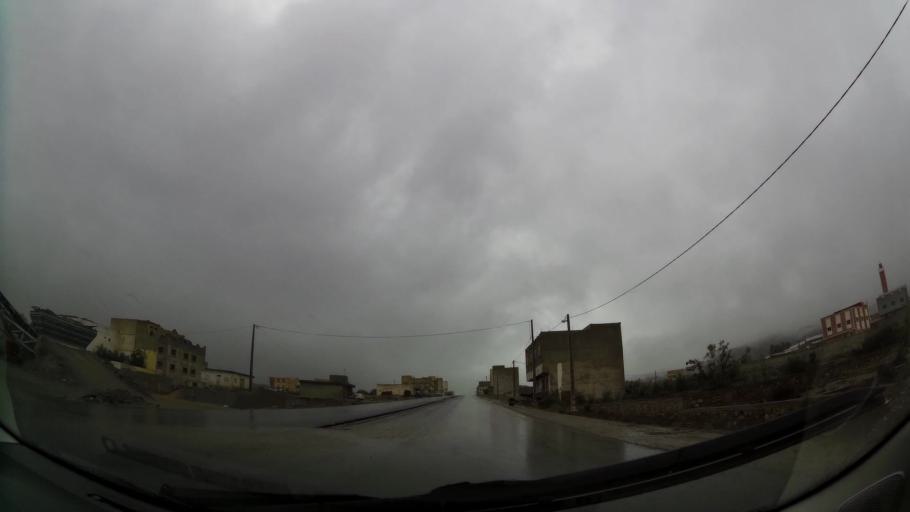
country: MA
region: Taza-Al Hoceima-Taounate
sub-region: Taza
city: Aknoul
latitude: 34.8194
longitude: -3.7268
